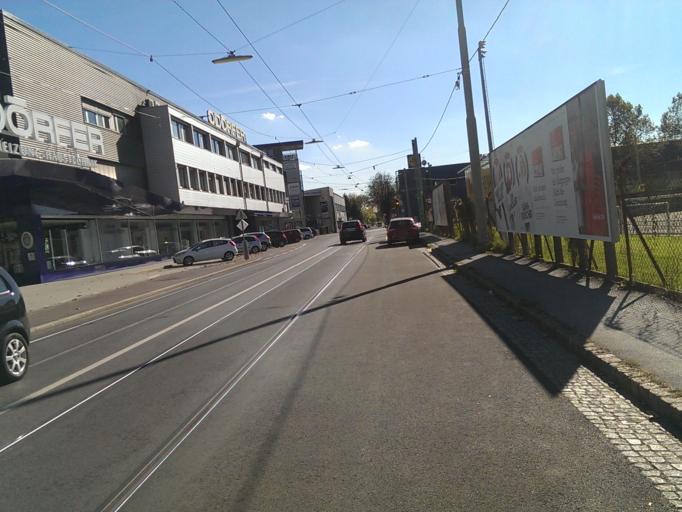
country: AT
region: Styria
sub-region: Graz Stadt
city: Graz
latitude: 47.0470
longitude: 15.4329
